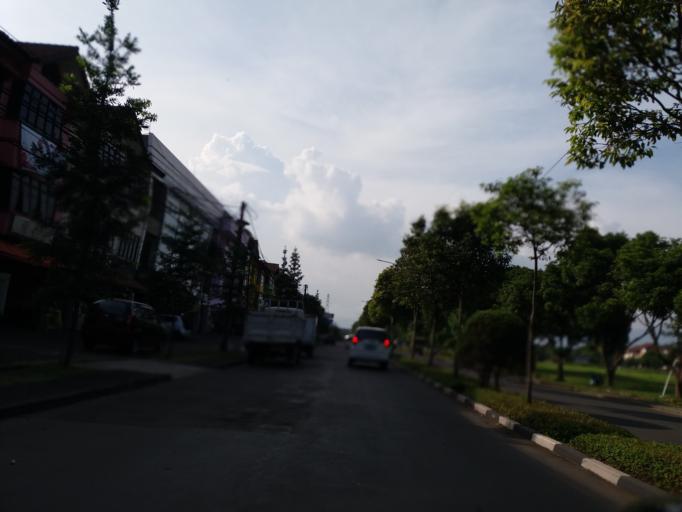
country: ID
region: West Java
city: Bandung
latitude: -6.9577
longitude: 107.6266
